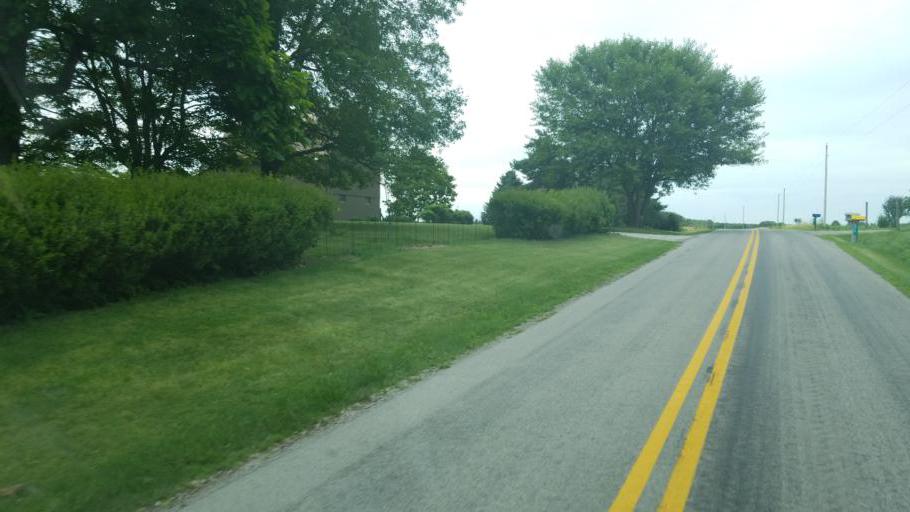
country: US
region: Ohio
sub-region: Delaware County
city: Ashley
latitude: 40.4154
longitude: -83.0081
